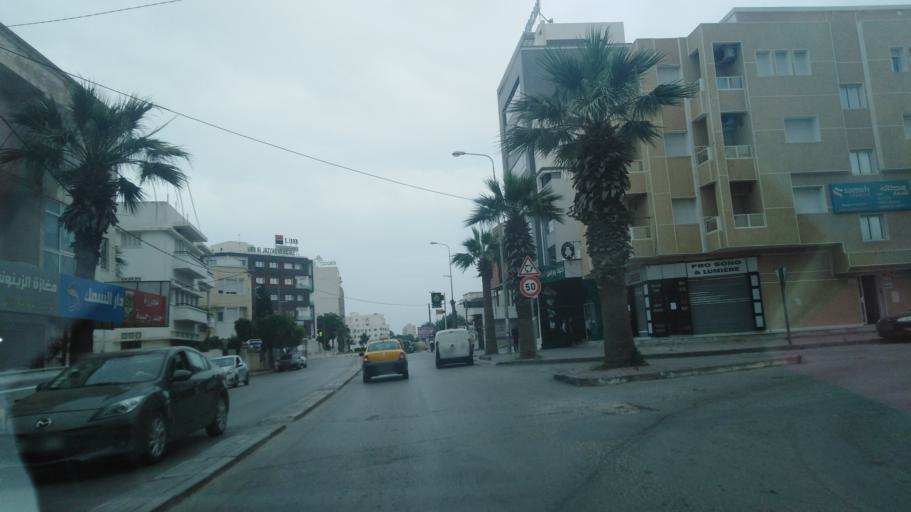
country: TN
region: Susah
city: Sousse
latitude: 35.8315
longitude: 10.6249
